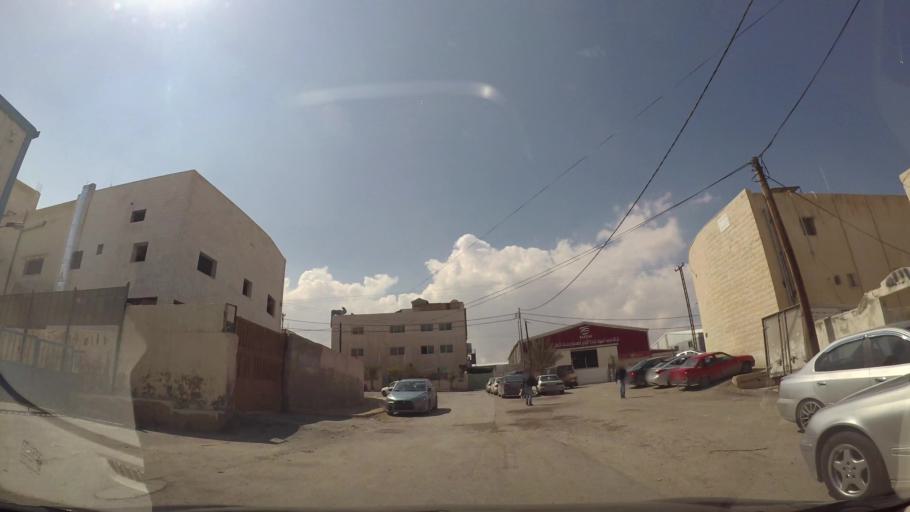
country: JO
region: Zarqa
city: Russeifa
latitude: 31.9874
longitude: 36.0147
